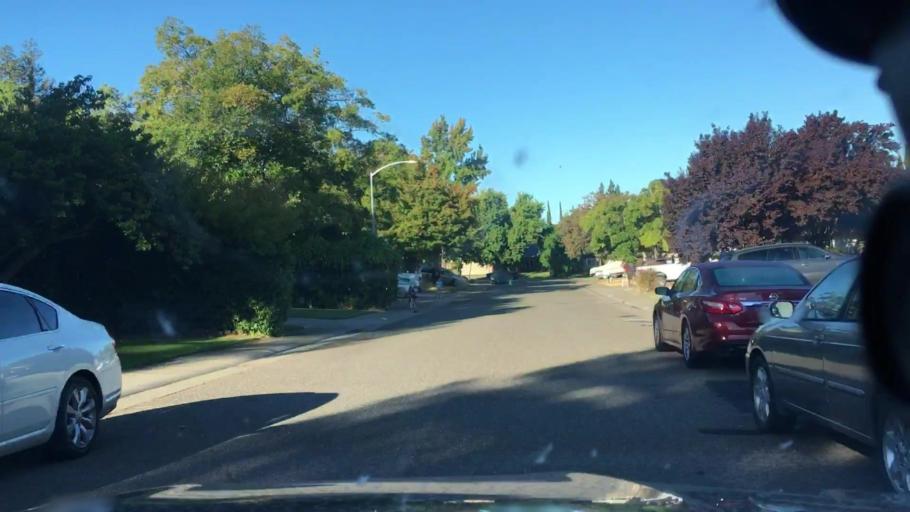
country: US
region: California
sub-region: Sacramento County
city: Antelope
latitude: 38.7050
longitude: -121.3404
